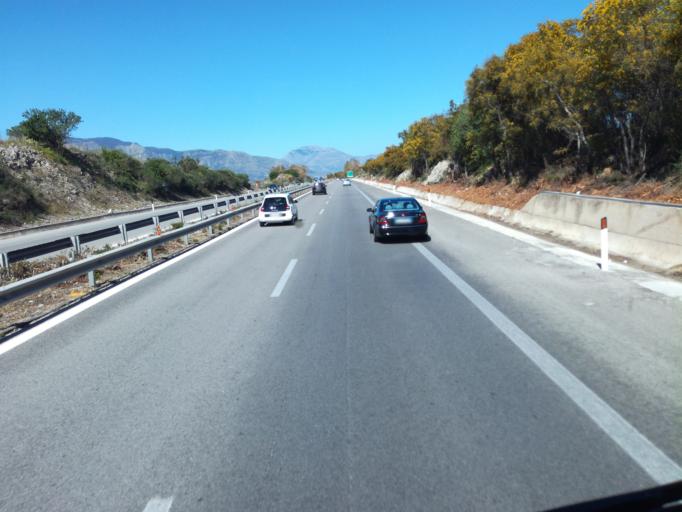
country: IT
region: Sicily
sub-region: Trapani
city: Alcamo
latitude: 38.0170
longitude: 12.9761
